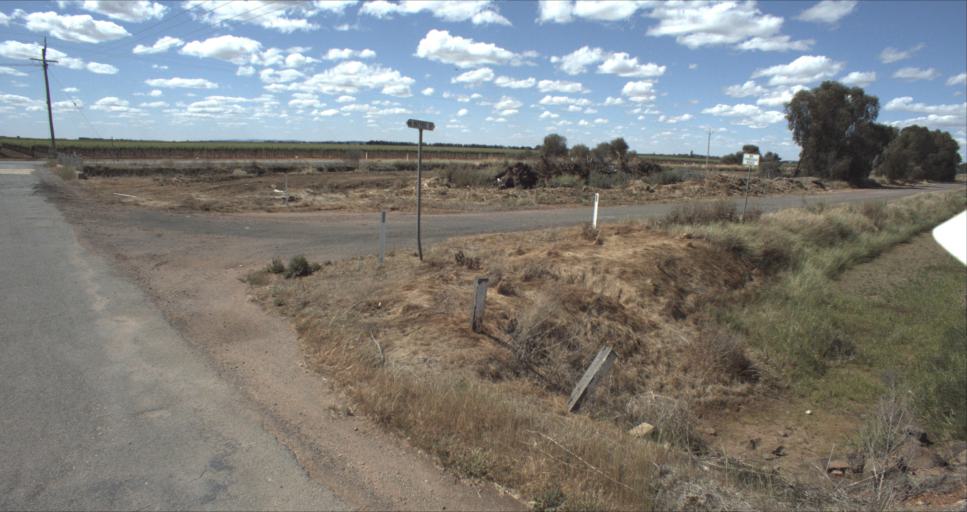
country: AU
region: New South Wales
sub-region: Leeton
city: Leeton
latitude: -34.5057
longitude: 146.2215
